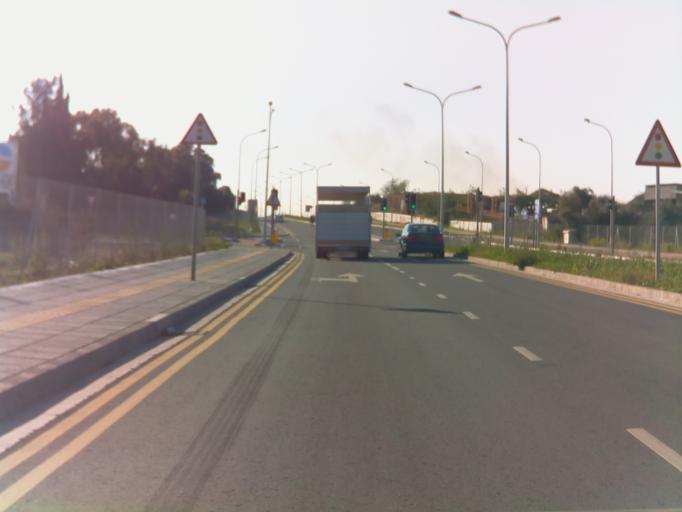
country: CY
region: Limassol
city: Ypsonas
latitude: 34.6718
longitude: 32.9889
